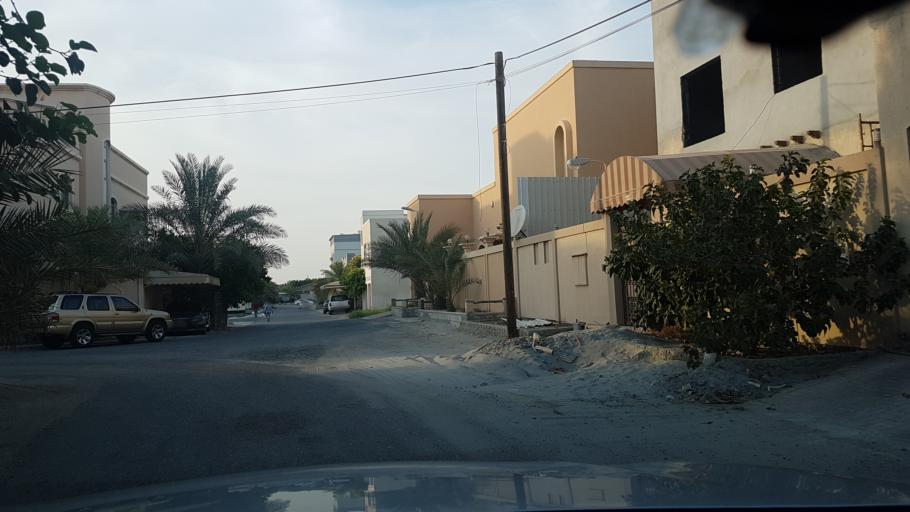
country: BH
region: Manama
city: Jidd Hafs
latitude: 26.2181
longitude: 50.4739
